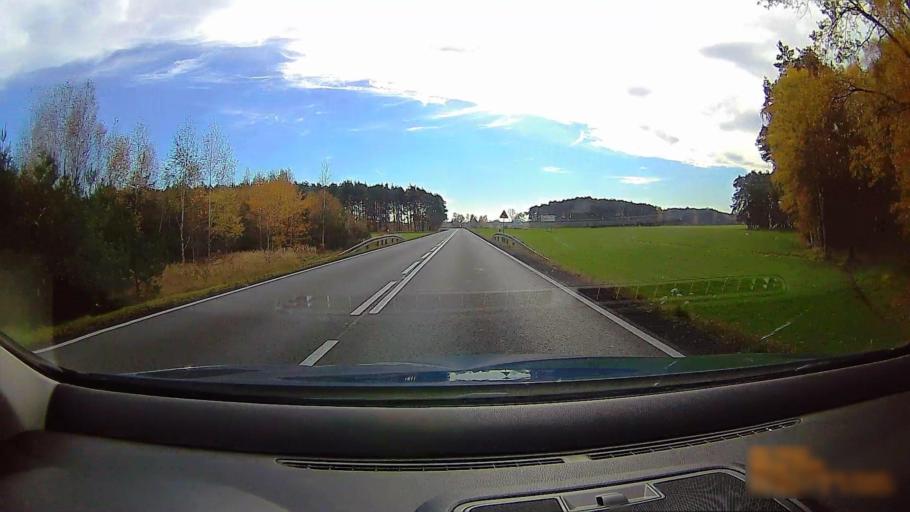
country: PL
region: Greater Poland Voivodeship
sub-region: Powiat ostrowski
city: Przygodzice
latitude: 51.4931
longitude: 17.8539
